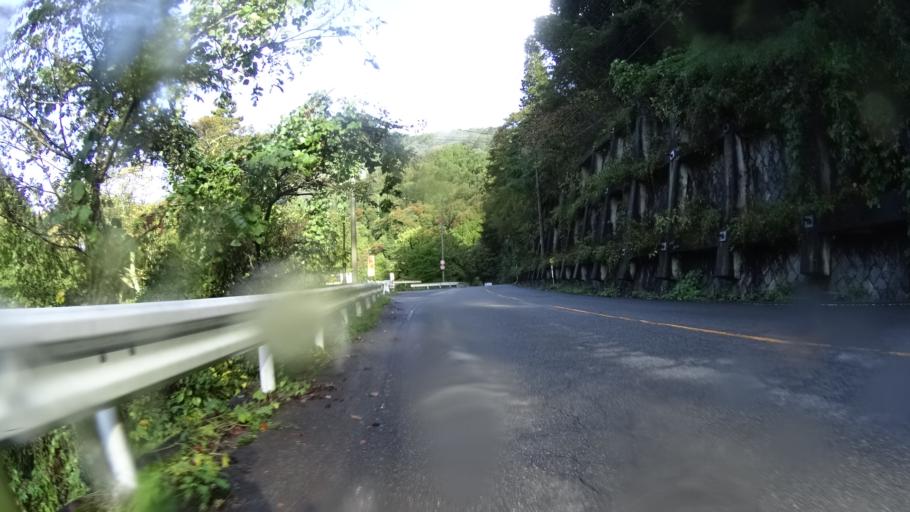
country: JP
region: Yamanashi
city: Otsuki
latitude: 35.7822
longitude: 138.9775
